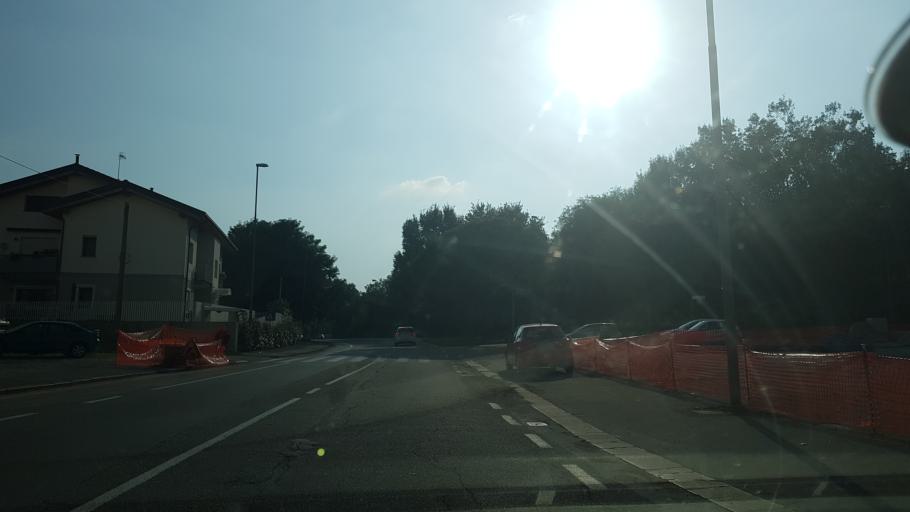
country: IT
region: Friuli Venezia Giulia
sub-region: Provincia di Gorizia
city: Gorizia
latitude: 45.9395
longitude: 13.6348
